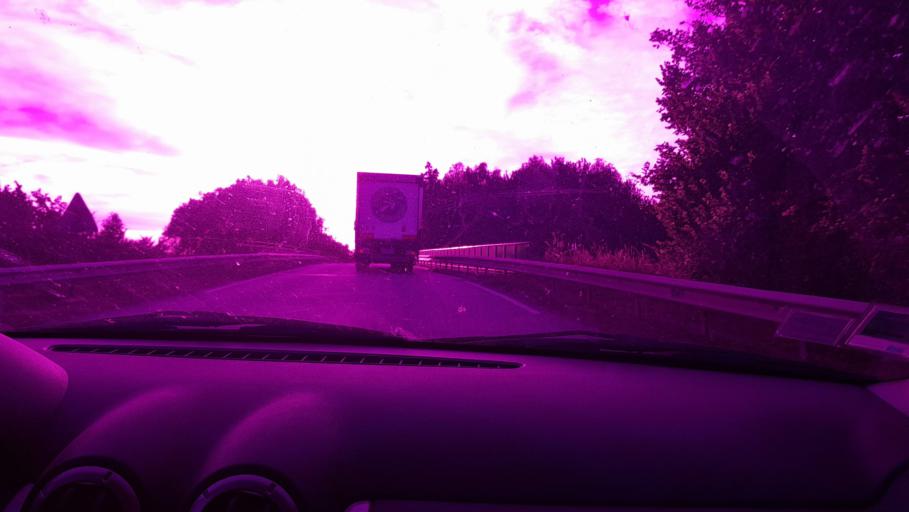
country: FR
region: Brittany
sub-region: Departement d'Ille-et-Vilaine
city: Erbree
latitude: 48.0883
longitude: -1.1058
